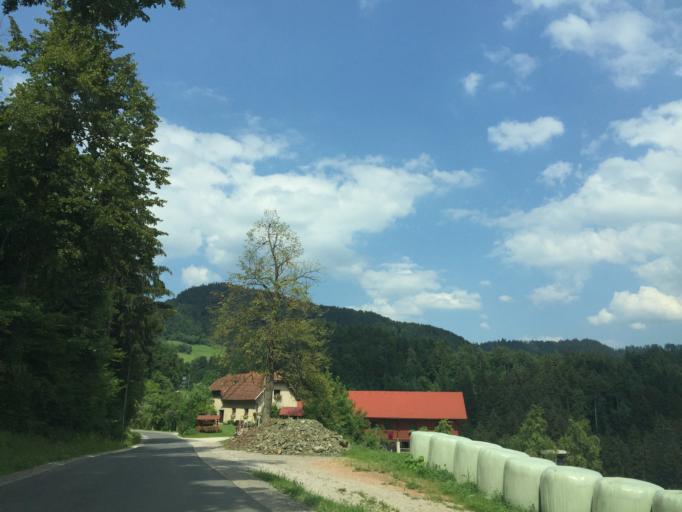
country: SI
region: Sostanj
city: Ravne
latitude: 46.4041
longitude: 15.0989
